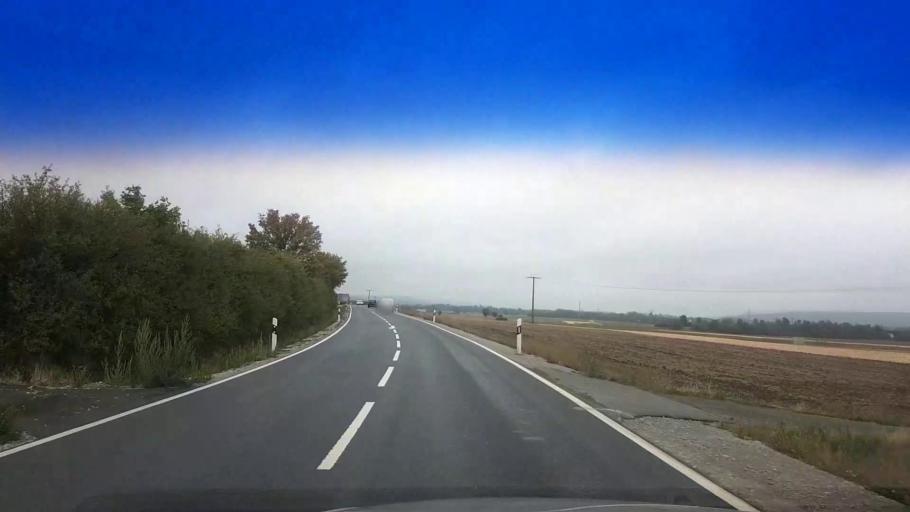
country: DE
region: Bavaria
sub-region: Upper Franconia
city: Buttenheim
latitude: 49.7907
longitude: 11.0388
